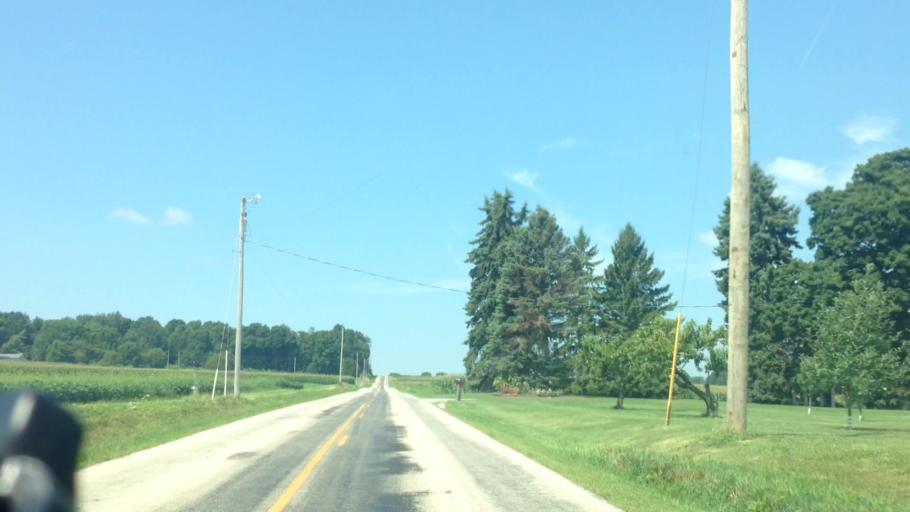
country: US
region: Ohio
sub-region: Wayne County
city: Orrville
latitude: 40.8739
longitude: -81.8072
